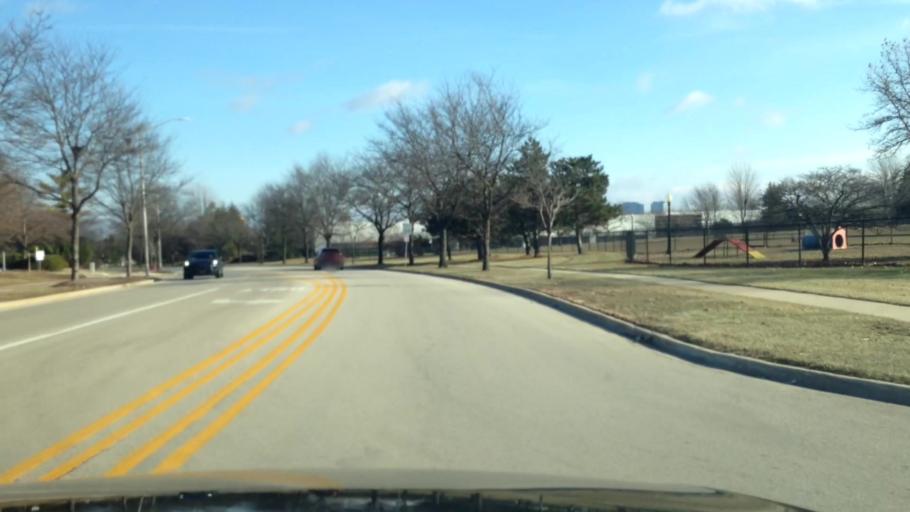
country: US
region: Illinois
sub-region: Cook County
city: Hoffman Estates
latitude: 42.0548
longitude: -88.0752
